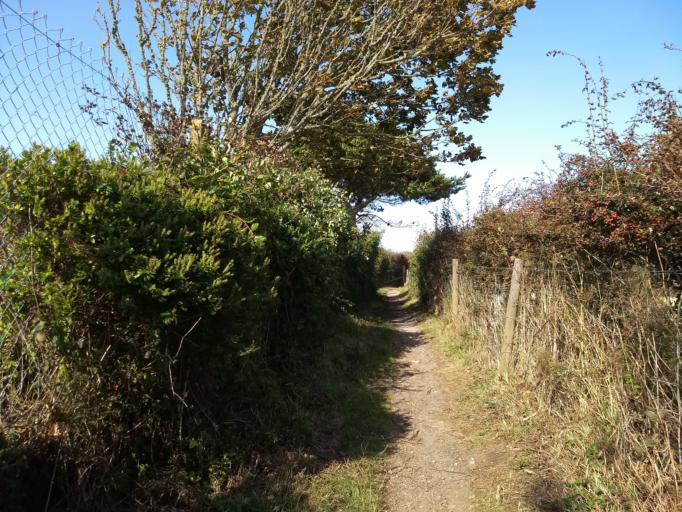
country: GB
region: England
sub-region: Isle of Wight
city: Totland
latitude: 50.7002
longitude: -1.5306
